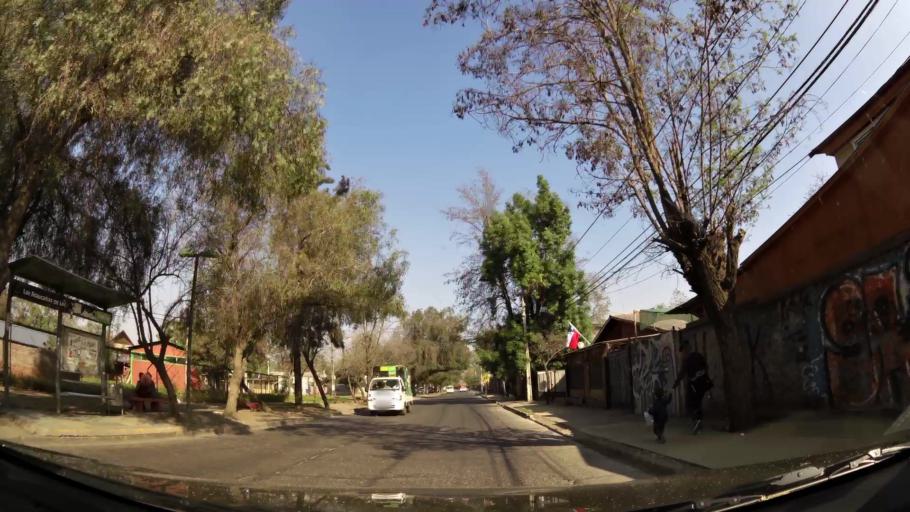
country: CL
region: Santiago Metropolitan
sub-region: Provincia de Santiago
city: Lo Prado
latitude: -33.3764
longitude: -70.6898
